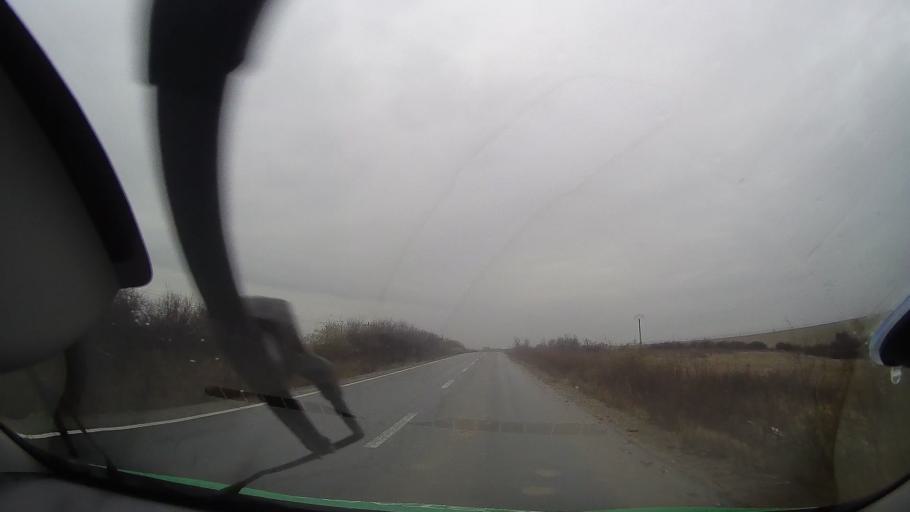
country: RO
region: Bihor
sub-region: Comuna Olcea
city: Olcea
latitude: 46.7099
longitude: 21.9596
